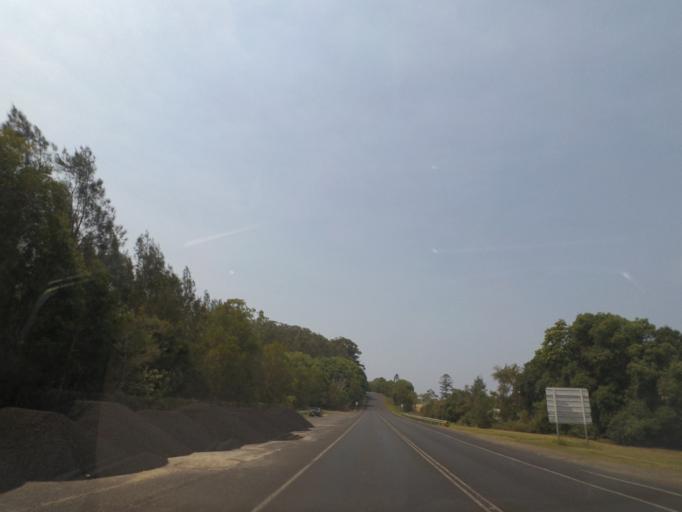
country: AU
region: New South Wales
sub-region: Byron Shire
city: Brunswick Heads
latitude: -28.5132
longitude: 153.5303
